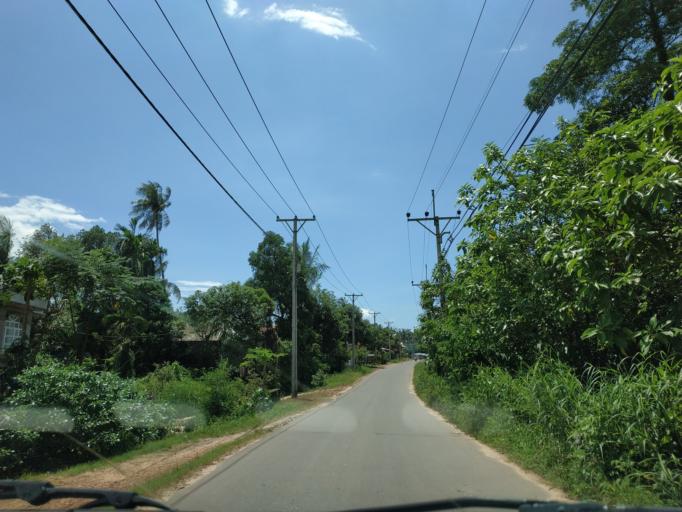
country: MM
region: Tanintharyi
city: Dawei
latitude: 14.0977
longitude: 98.1979
